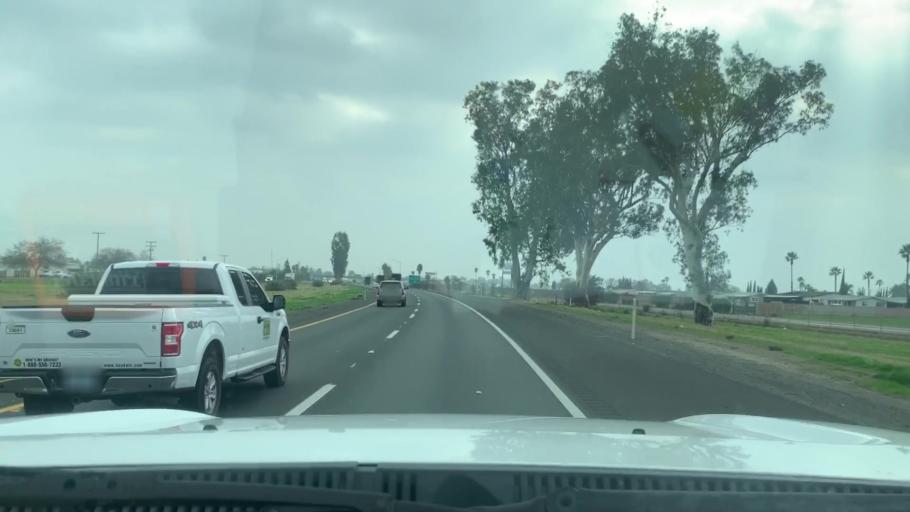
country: US
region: California
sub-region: Tulare County
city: Tulare
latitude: 36.1586
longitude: -119.3333
